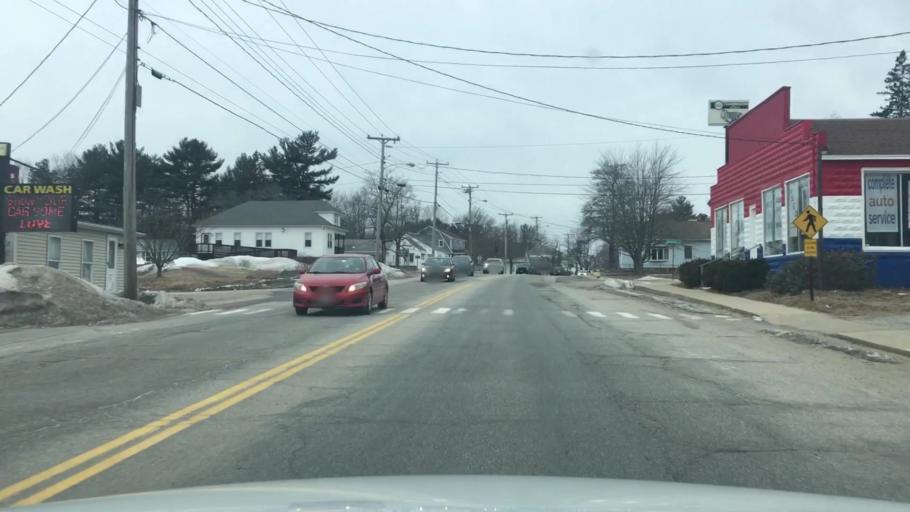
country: US
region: Maine
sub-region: York County
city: Sanford (historical)
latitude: 43.4268
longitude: -70.7660
